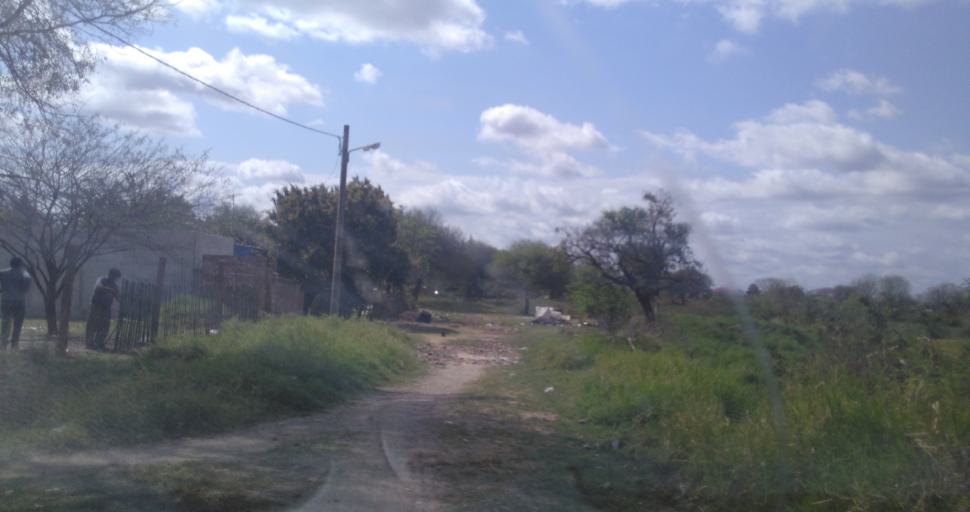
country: AR
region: Chaco
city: Fontana
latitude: -27.4289
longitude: -59.0321
